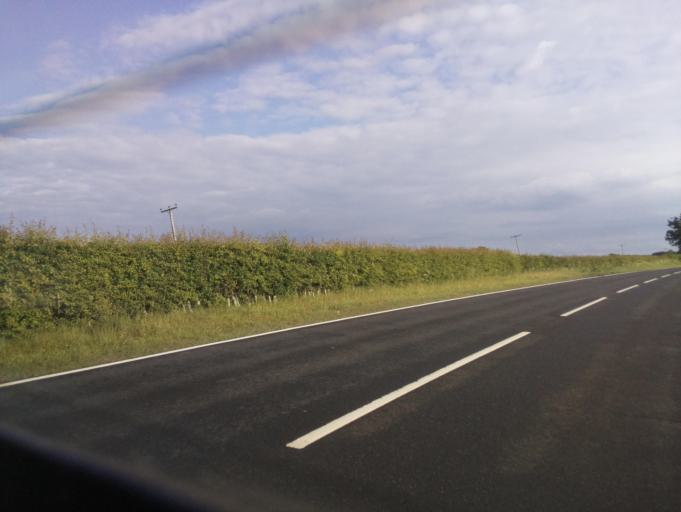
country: GB
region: England
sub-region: Lincolnshire
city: Navenby
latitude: 53.0667
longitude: -0.6360
